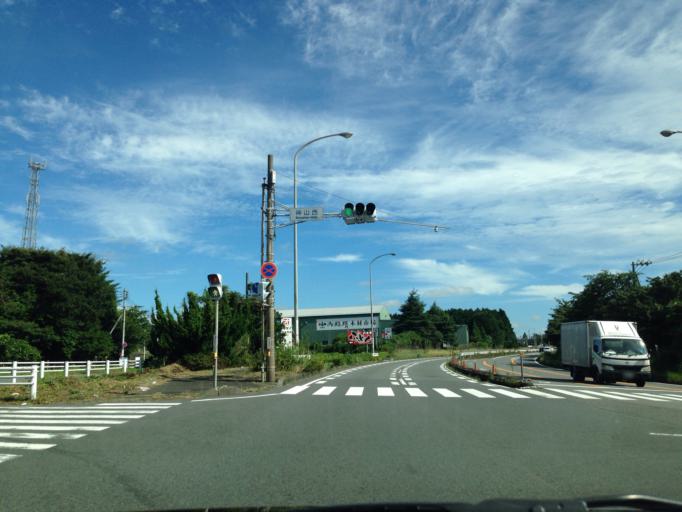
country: JP
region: Shizuoka
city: Gotemba
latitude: 35.2351
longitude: 138.9099
